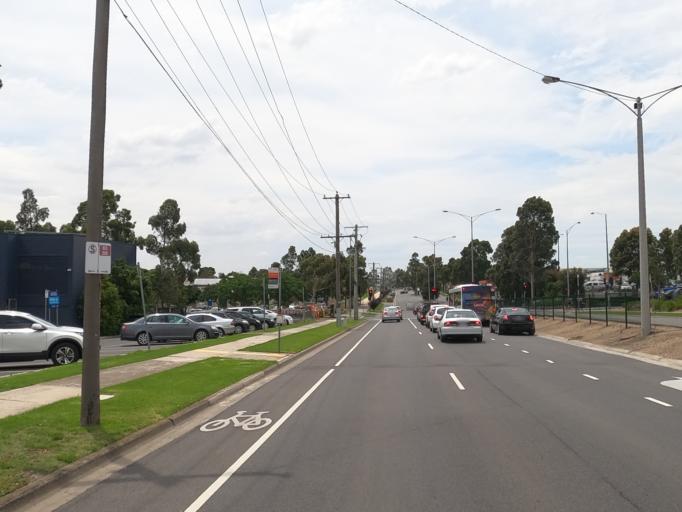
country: AU
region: Victoria
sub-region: Hume
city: Broadmeadows
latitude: -37.6816
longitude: 144.9160
